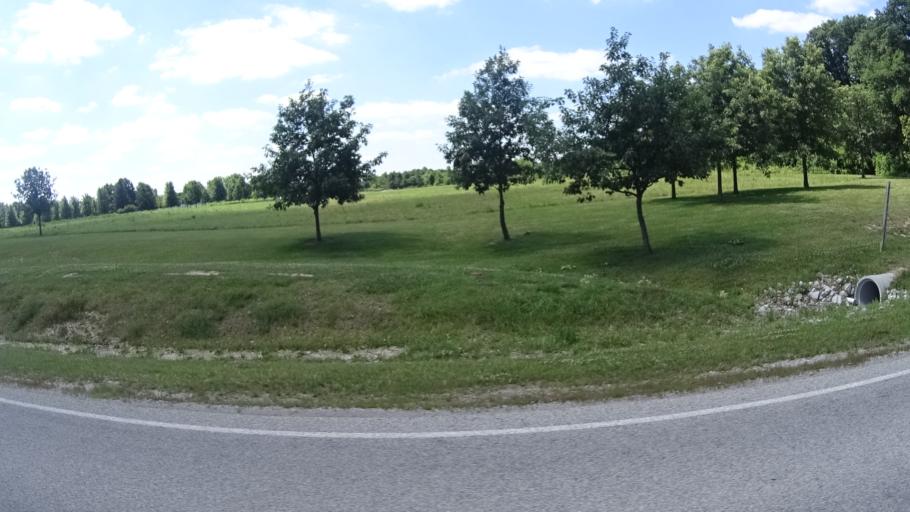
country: US
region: Ohio
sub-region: Erie County
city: Huron
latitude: 41.4025
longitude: -82.5964
